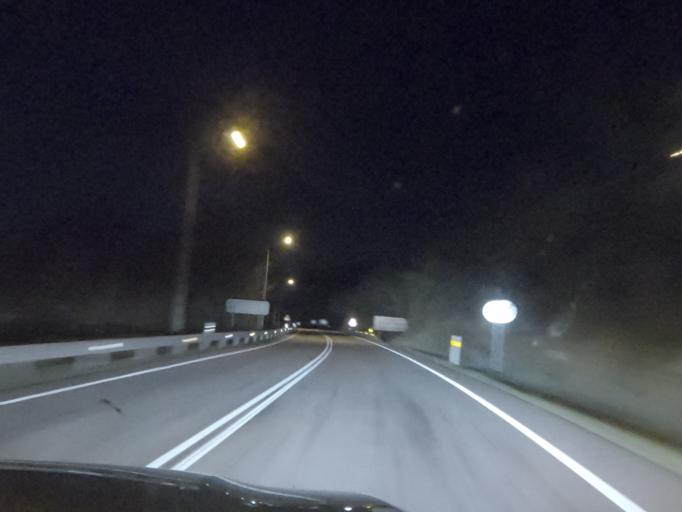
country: ES
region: Galicia
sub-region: Provincia de Ourense
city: Cualedro
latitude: 41.9687
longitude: -7.5196
